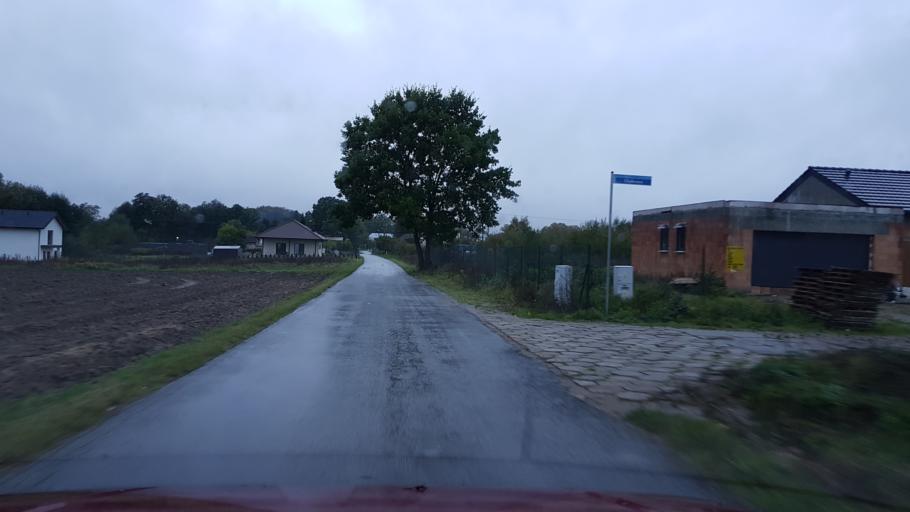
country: PL
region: West Pomeranian Voivodeship
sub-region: Koszalin
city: Koszalin
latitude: 54.1329
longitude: 16.1235
